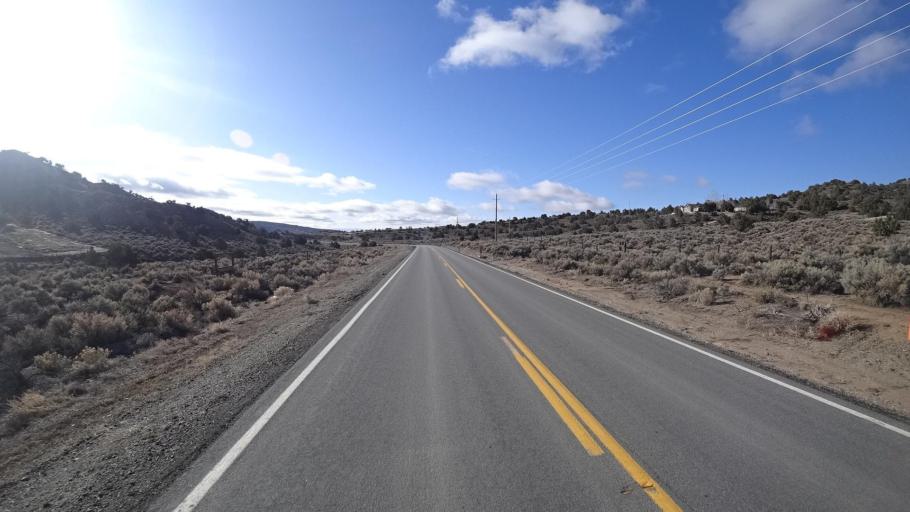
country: US
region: Nevada
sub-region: Washoe County
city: Cold Springs
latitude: 39.7374
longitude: -119.8839
